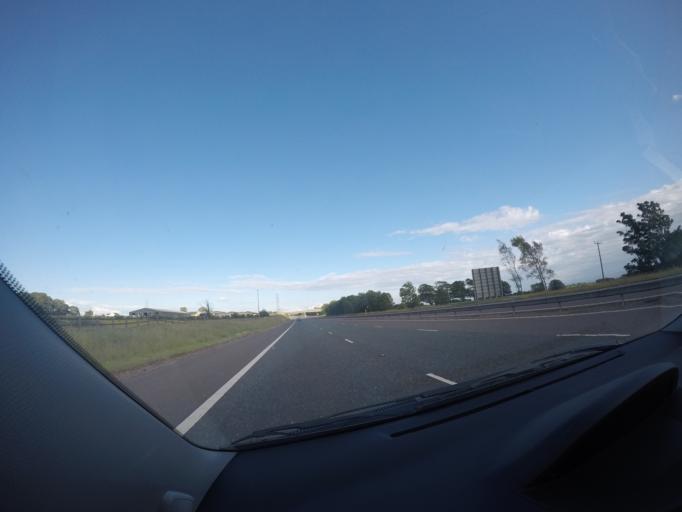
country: GB
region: Scotland
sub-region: Dumfries and Galloway
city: Gretna
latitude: 55.0144
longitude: -3.1046
